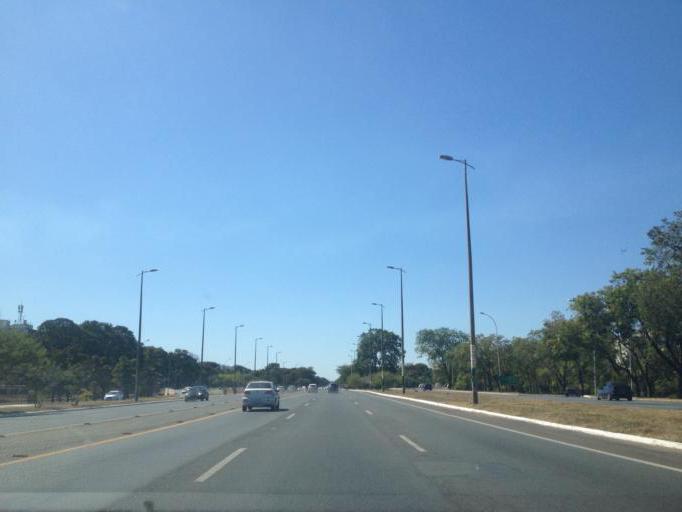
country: BR
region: Federal District
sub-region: Brasilia
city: Brasilia
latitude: -15.8359
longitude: -47.9268
